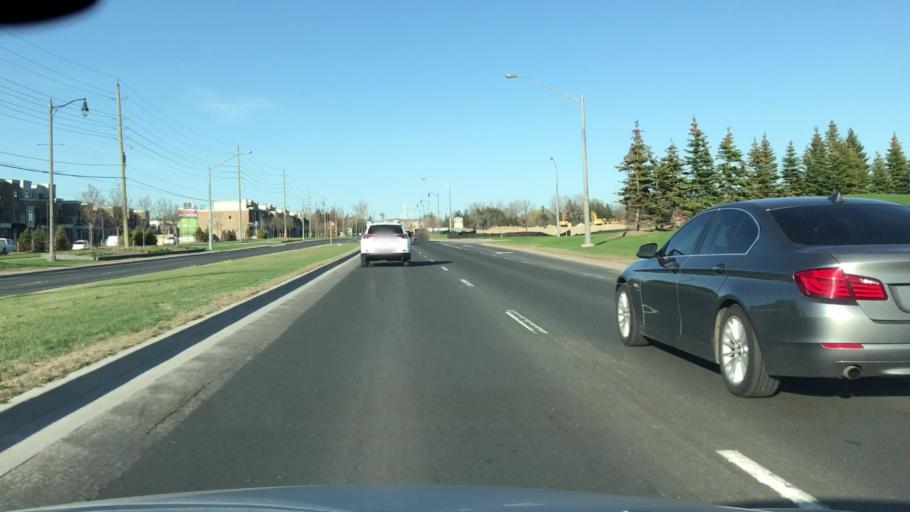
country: CA
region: Ontario
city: Newmarket
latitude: 44.0082
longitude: -79.4301
